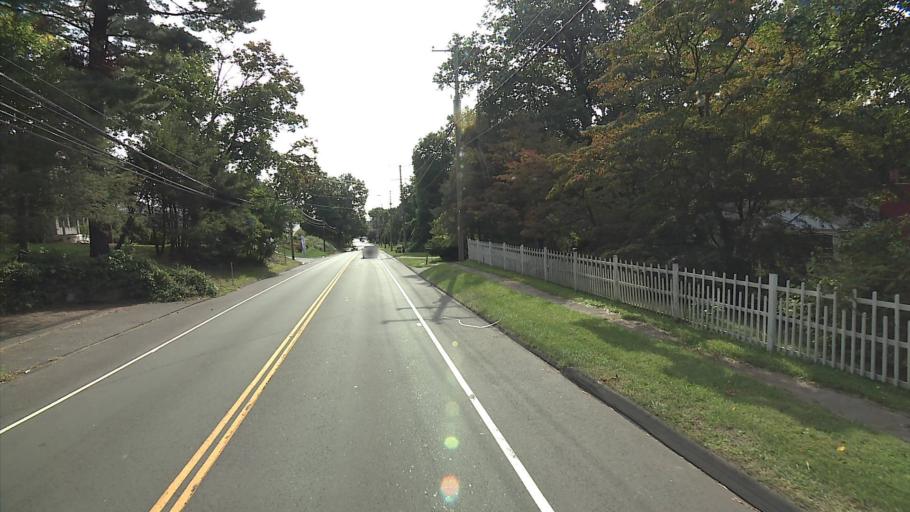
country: US
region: Connecticut
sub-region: Fairfield County
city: Norwalk
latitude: 41.1295
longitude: -73.4405
